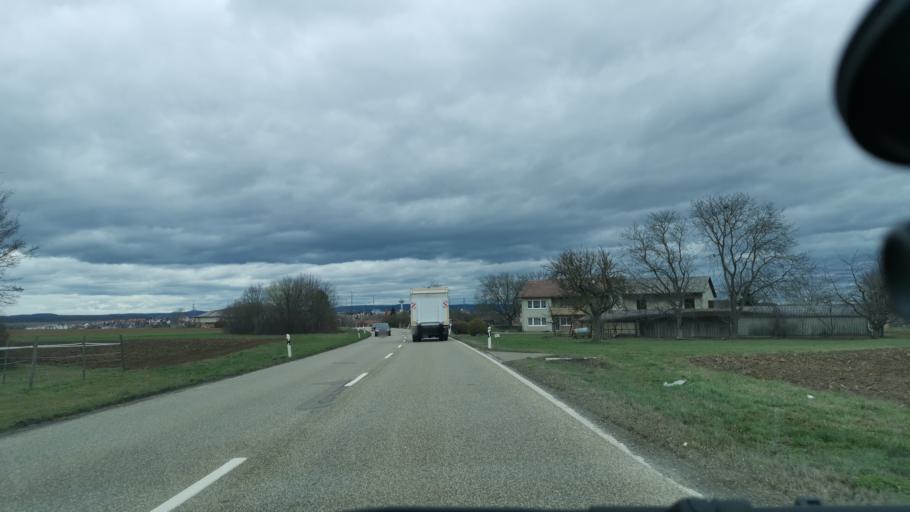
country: DE
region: Baden-Wuerttemberg
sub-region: Regierungsbezirk Stuttgart
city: Markgroningen
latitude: 48.8933
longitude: 9.0889
